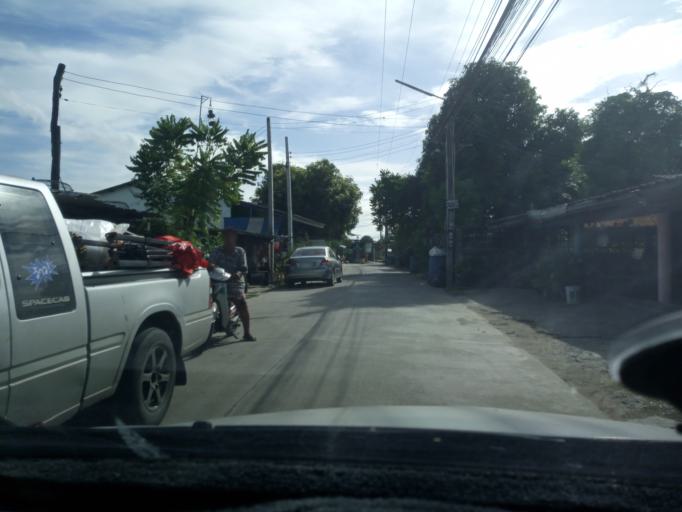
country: TH
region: Chon Buri
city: Phan Thong
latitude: 13.4202
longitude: 101.0628
